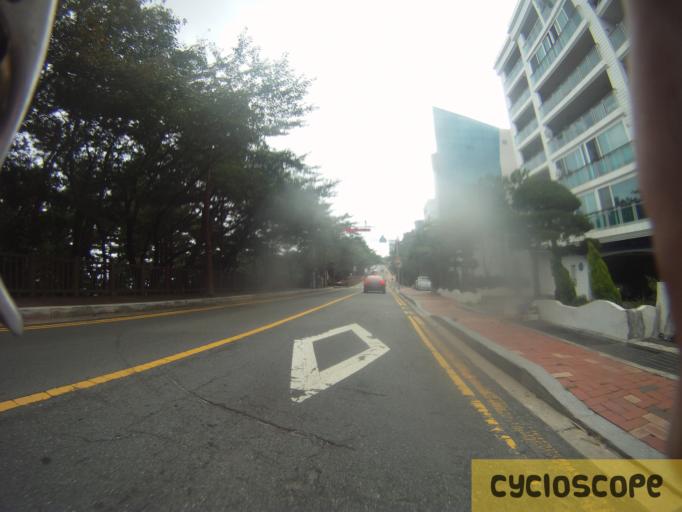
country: KR
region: Busan
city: Kijang
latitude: 35.1583
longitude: 129.1826
